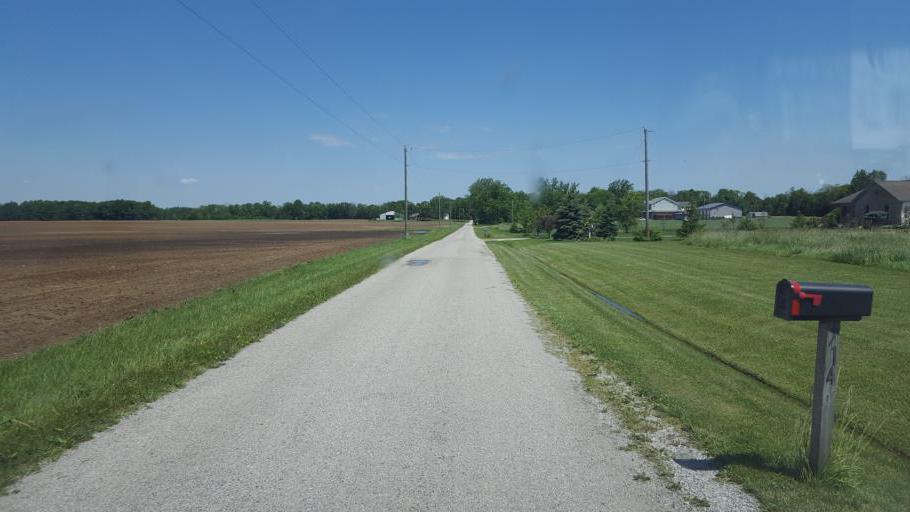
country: US
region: Ohio
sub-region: Union County
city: Richwood
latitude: 40.5770
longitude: -83.3951
